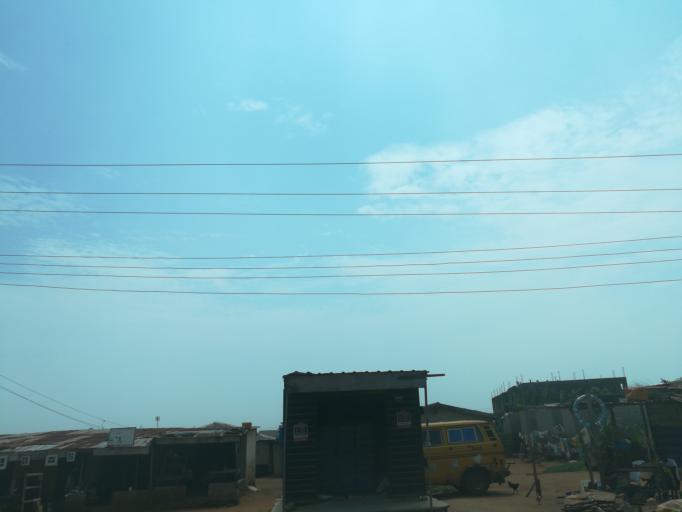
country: NG
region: Lagos
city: Ikorodu
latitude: 6.5840
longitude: 3.6256
